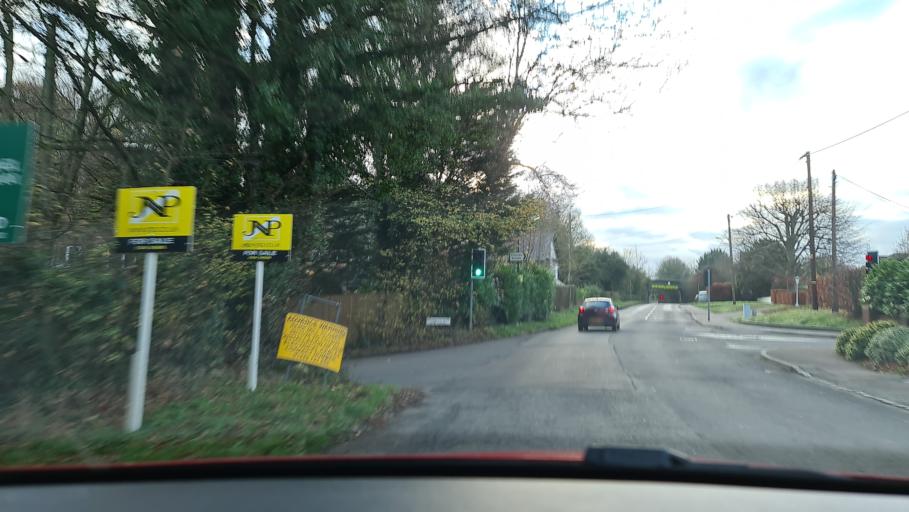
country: GB
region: England
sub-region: Buckinghamshire
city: Princes Risborough
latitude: 51.7232
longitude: -0.8455
